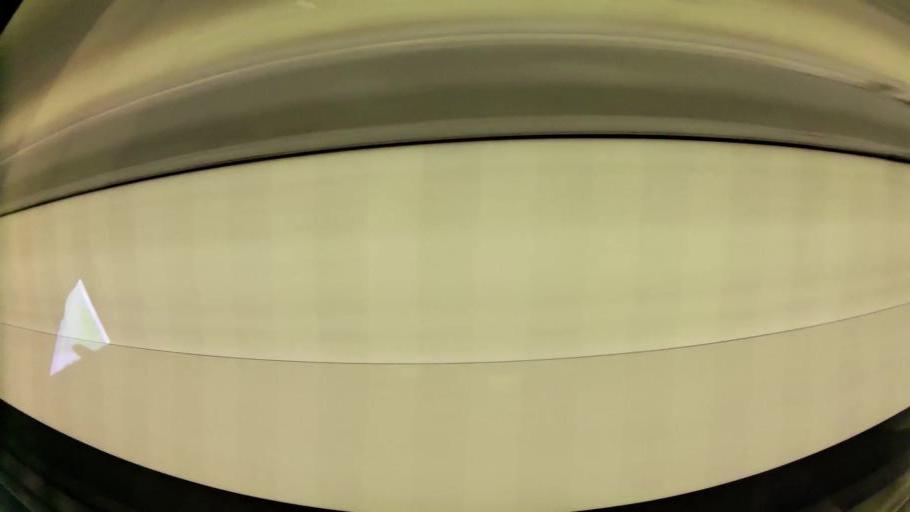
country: HK
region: Tsuen Wan
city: Tsuen Wan
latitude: 22.3780
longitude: 114.1427
